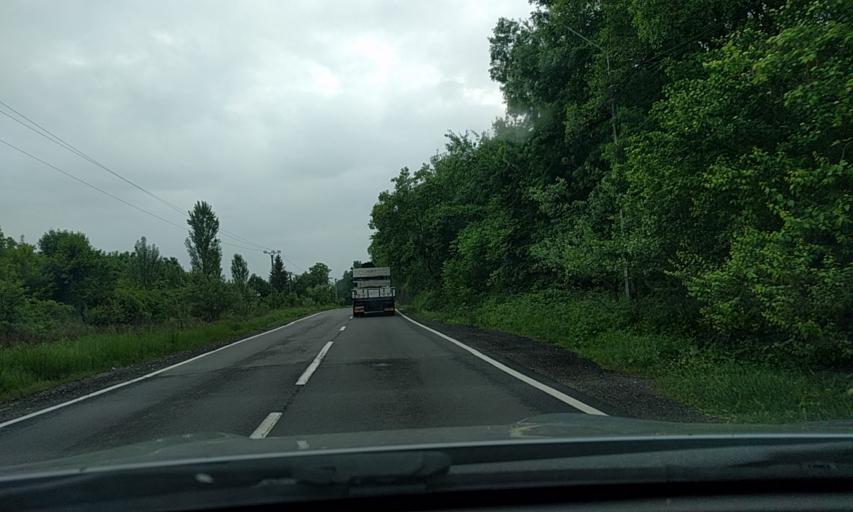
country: RO
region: Dambovita
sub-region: Comuna Vulcana-Pandele
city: Vulcana-Pandele
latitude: 45.0143
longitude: 25.4070
